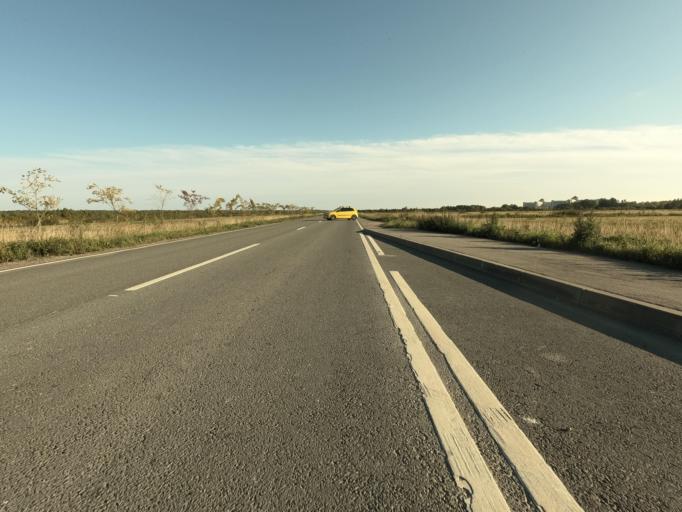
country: RU
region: St.-Petersburg
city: Sapernyy
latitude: 59.7539
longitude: 30.6334
